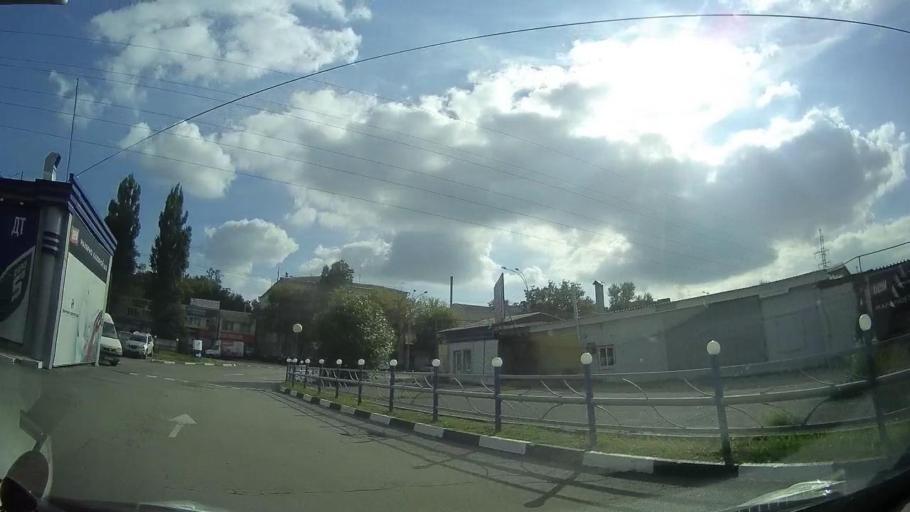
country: RU
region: Rostov
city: Imeni Chkalova
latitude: 47.2498
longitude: 39.7768
